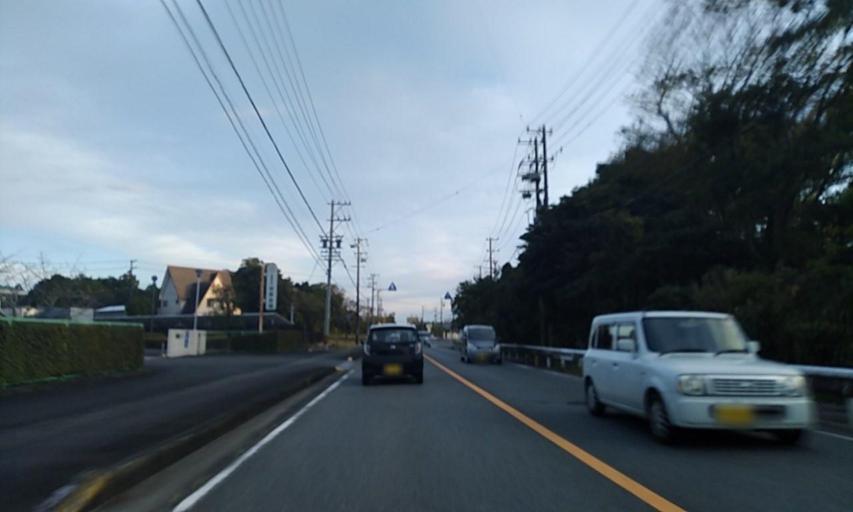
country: JP
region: Mie
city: Toba
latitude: 34.3171
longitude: 136.8563
